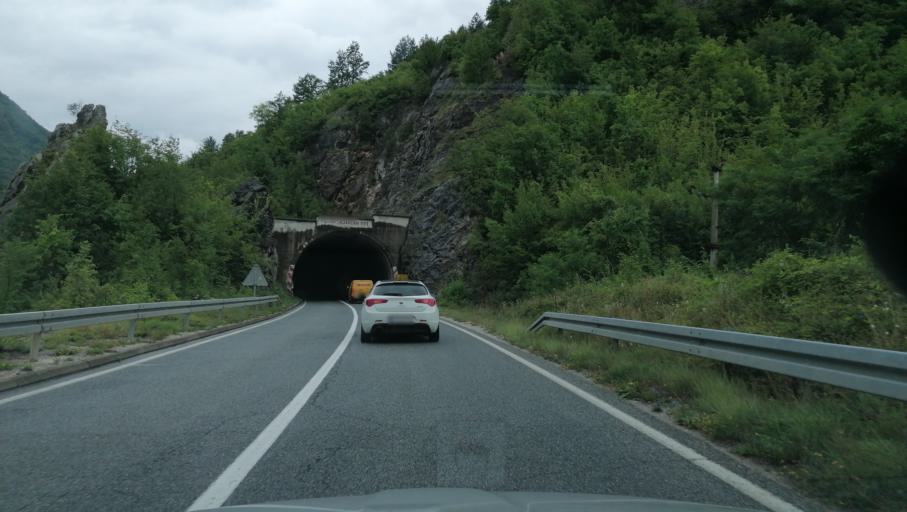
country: BA
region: Republika Srpska
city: Visegrad
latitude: 43.7540
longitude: 19.2413
